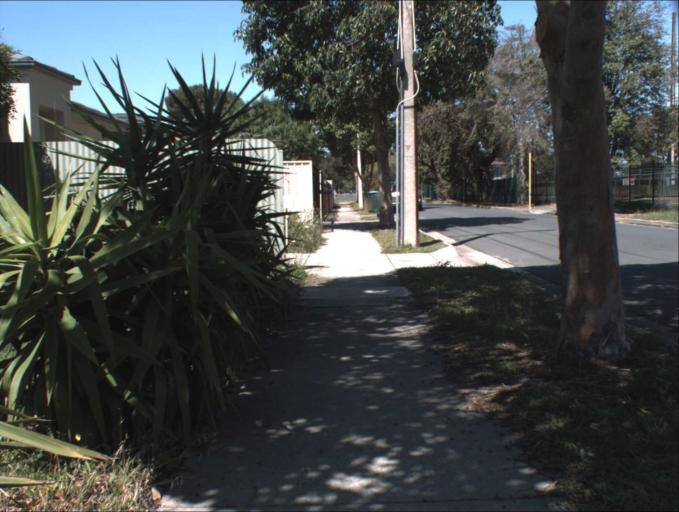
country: AU
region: South Australia
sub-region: Port Adelaide Enfield
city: Birkenhead
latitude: -34.8134
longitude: 138.4992
